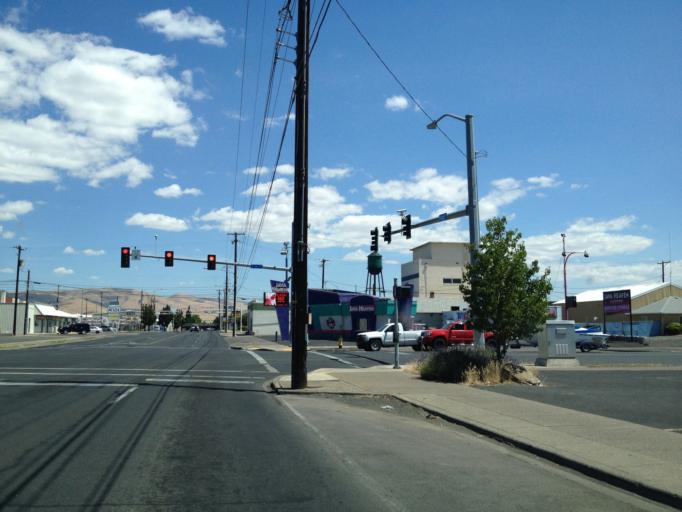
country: US
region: Washington
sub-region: Yakima County
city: Yakima
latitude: 46.5980
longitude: -120.5120
